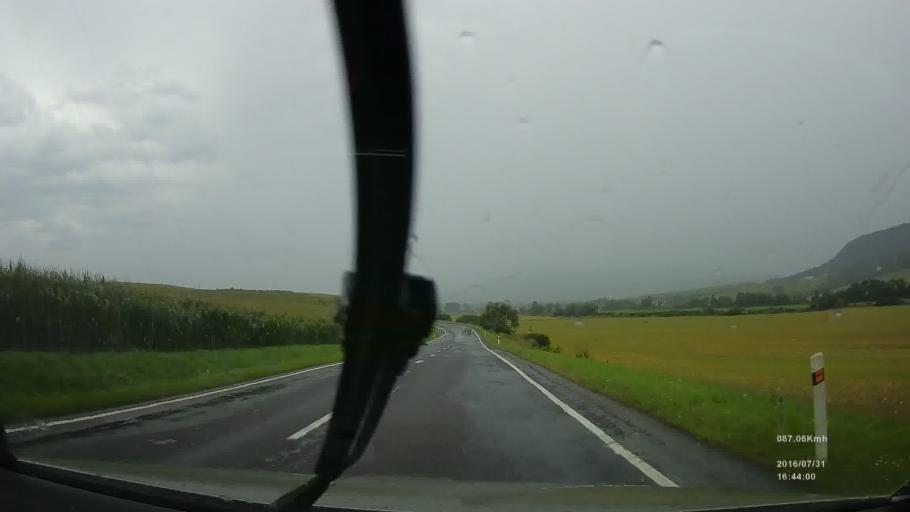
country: SK
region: Presovsky
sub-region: Okres Presov
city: Presov
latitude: 49.0797
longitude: 21.3196
